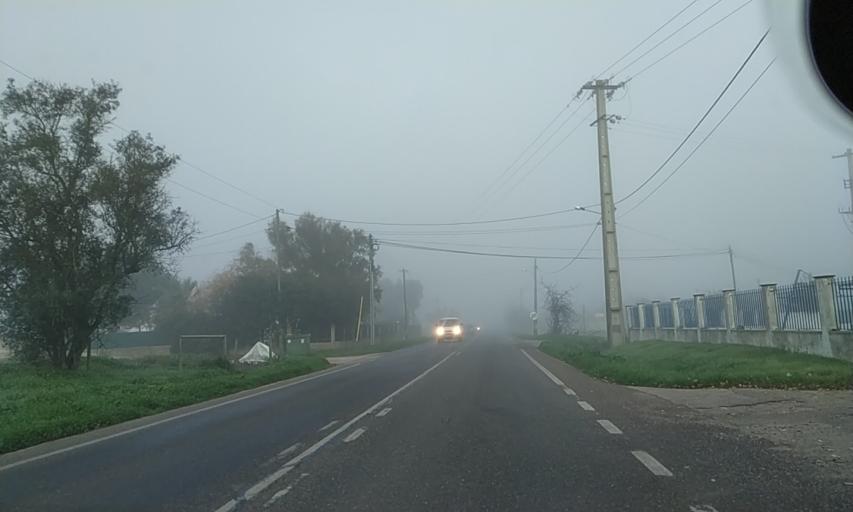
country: PT
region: Setubal
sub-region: Palmela
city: Pinhal Novo
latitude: 38.6138
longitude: -8.9117
